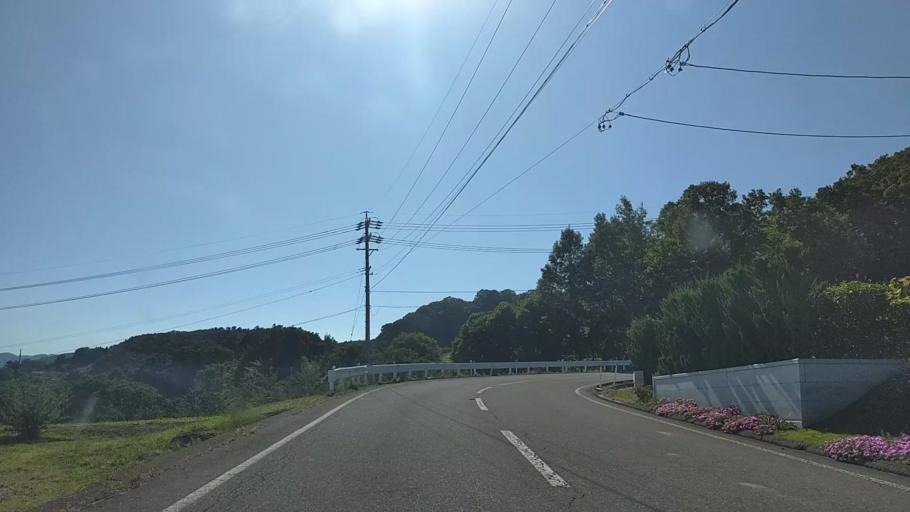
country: JP
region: Nagano
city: Nagano-shi
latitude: 36.5823
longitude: 138.1118
